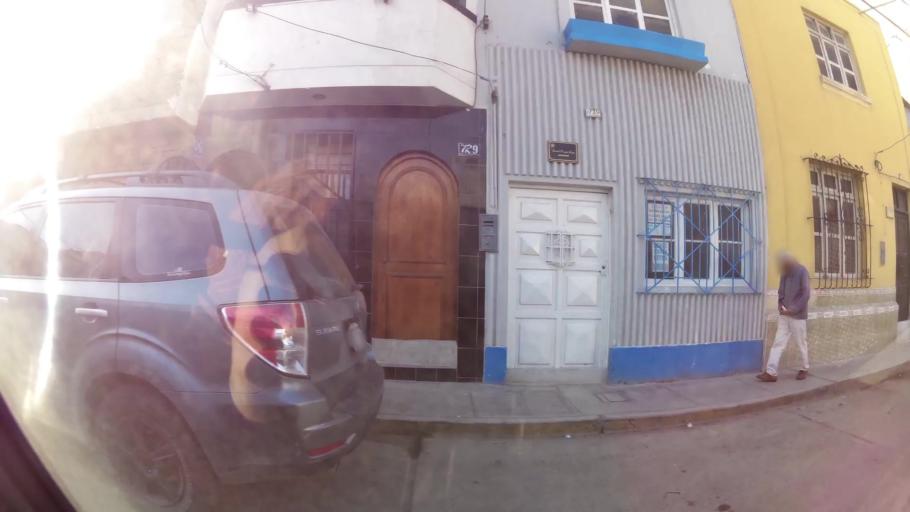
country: PE
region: Lambayeque
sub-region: Provincia de Chiclayo
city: Chiclayo
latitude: -6.7740
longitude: -79.8368
